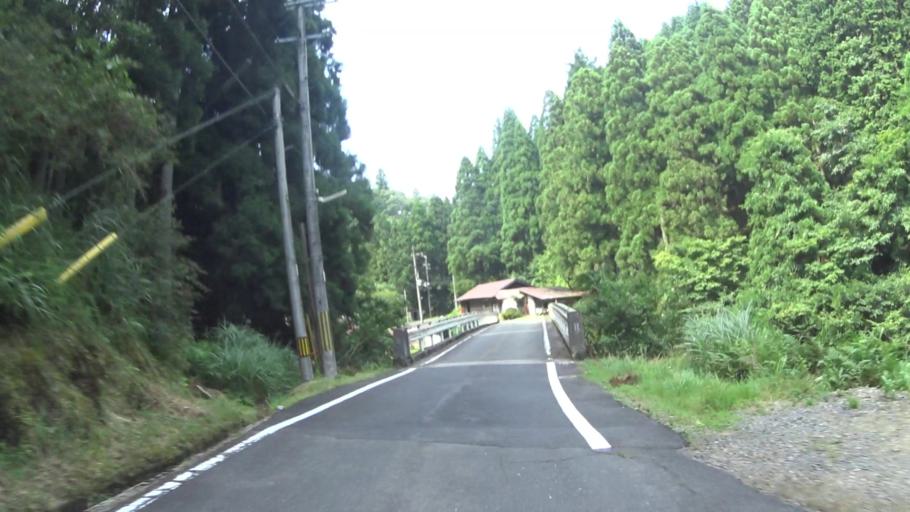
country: JP
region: Fukui
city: Obama
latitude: 35.3349
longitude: 135.6466
